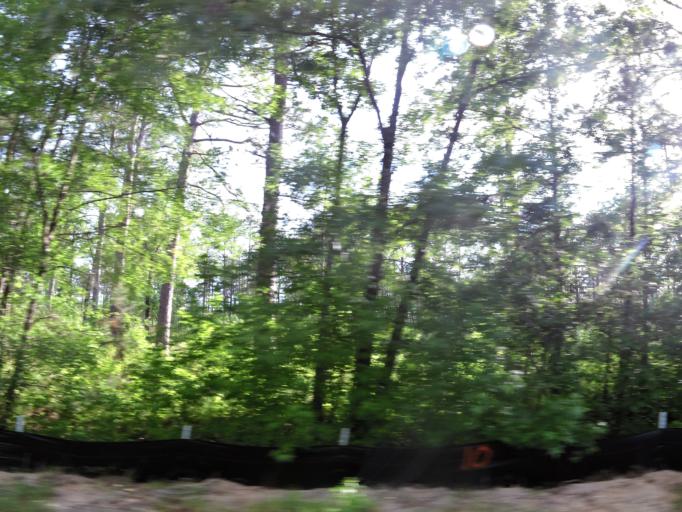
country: US
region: South Carolina
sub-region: Jasper County
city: Ridgeland
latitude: 32.5070
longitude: -81.1398
